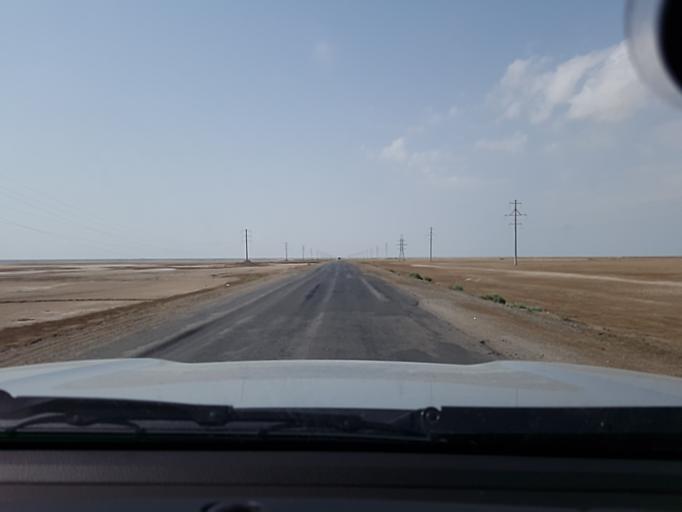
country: TM
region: Balkan
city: Gumdag
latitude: 39.0858
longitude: 54.5844
